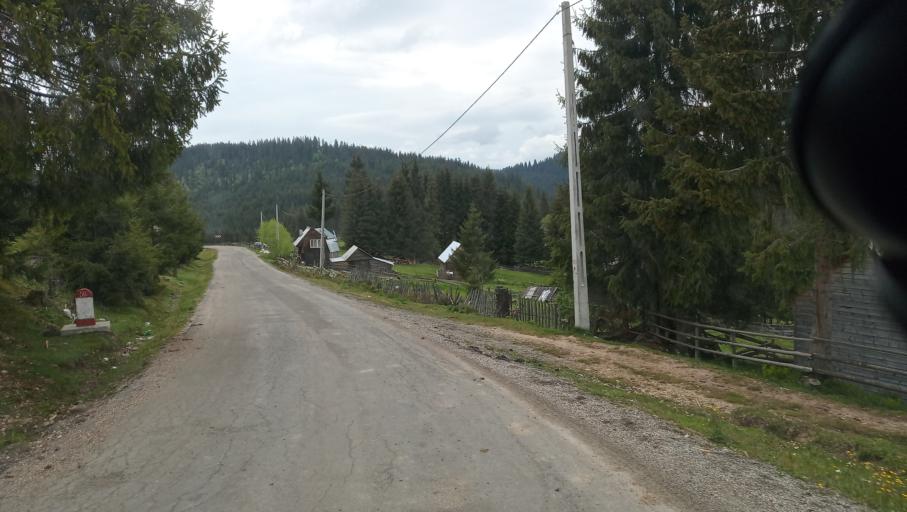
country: RO
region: Alba
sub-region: Comuna Horea
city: Horea
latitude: 46.5506
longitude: 22.8998
